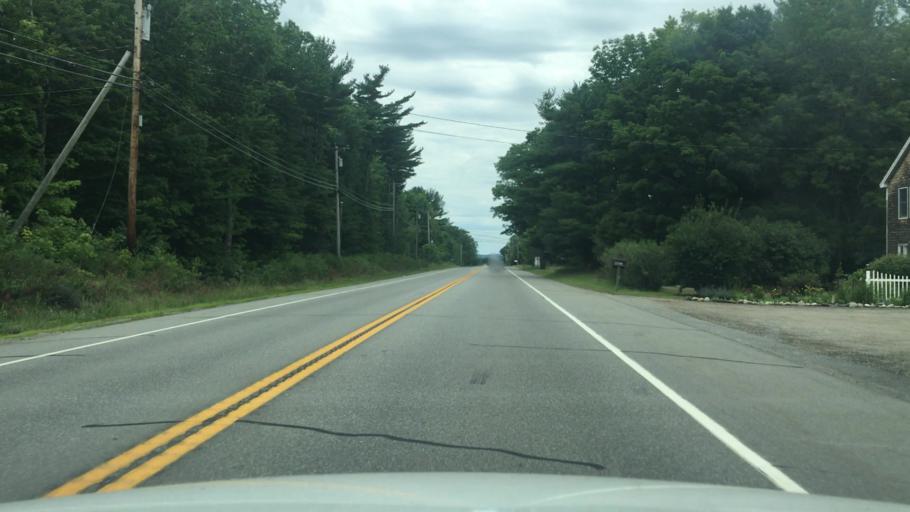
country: US
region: Maine
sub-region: Kennebec County
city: Sidney
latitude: 44.3358
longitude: -69.6831
